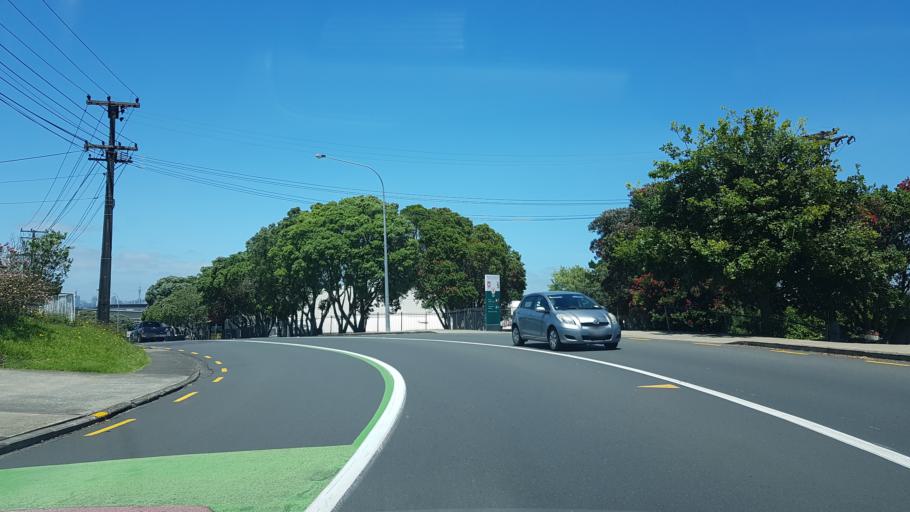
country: NZ
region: Auckland
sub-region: Auckland
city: North Shore
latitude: -36.7749
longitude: 174.7489
